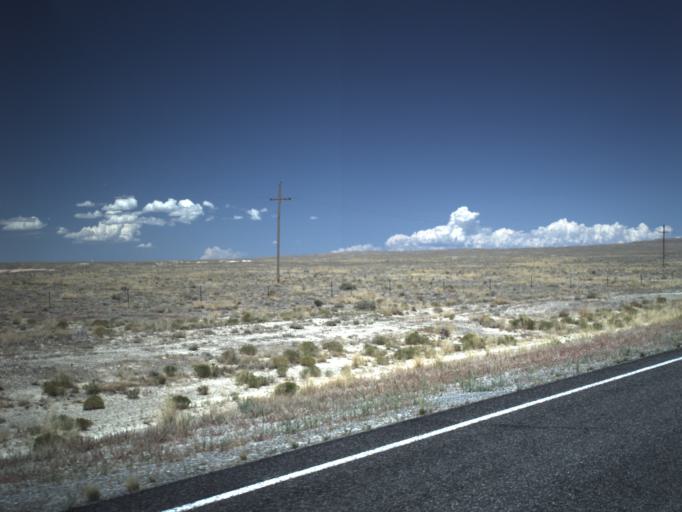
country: US
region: Utah
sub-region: Millard County
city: Delta
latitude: 39.1192
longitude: -113.1223
